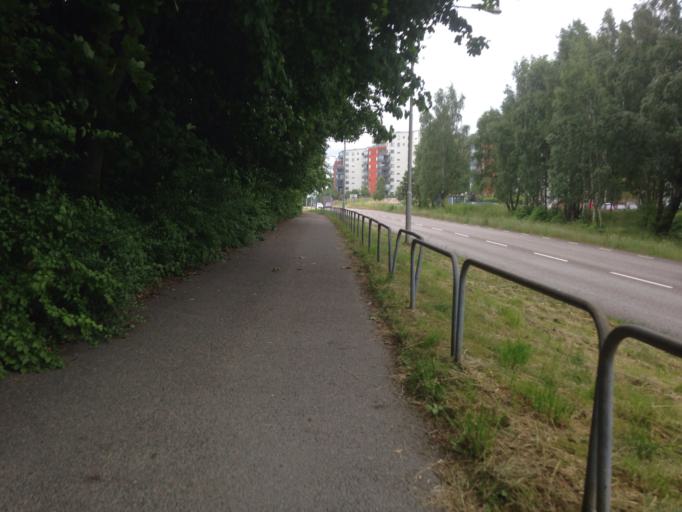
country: SE
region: Vaestra Goetaland
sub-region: Partille Kommun
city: Partille
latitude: 57.7198
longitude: 12.0613
